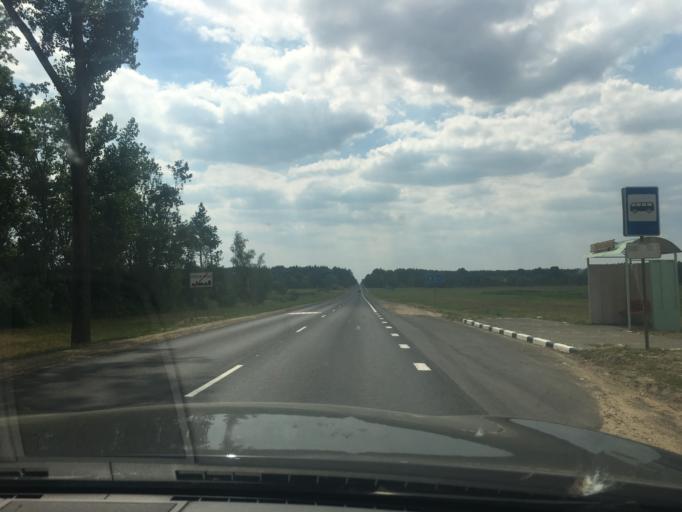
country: BY
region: Brest
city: Pruzhany
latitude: 52.5405
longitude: 24.4472
